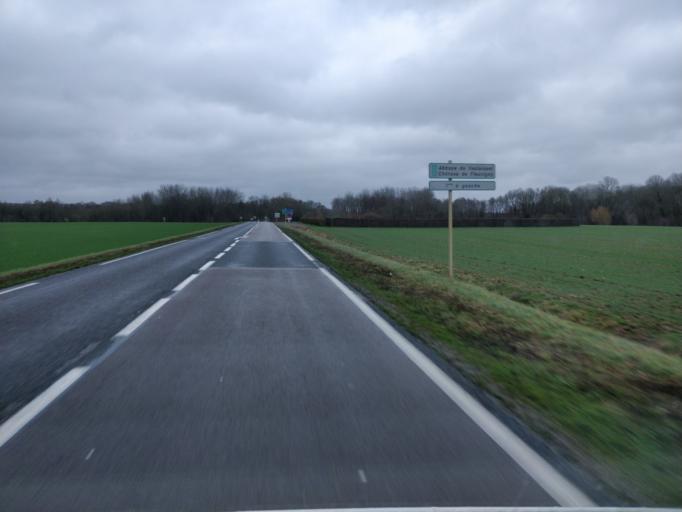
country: FR
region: Bourgogne
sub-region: Departement de l'Yonne
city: Thorigny-sur-Oreuse
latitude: 48.2332
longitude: 3.5271
